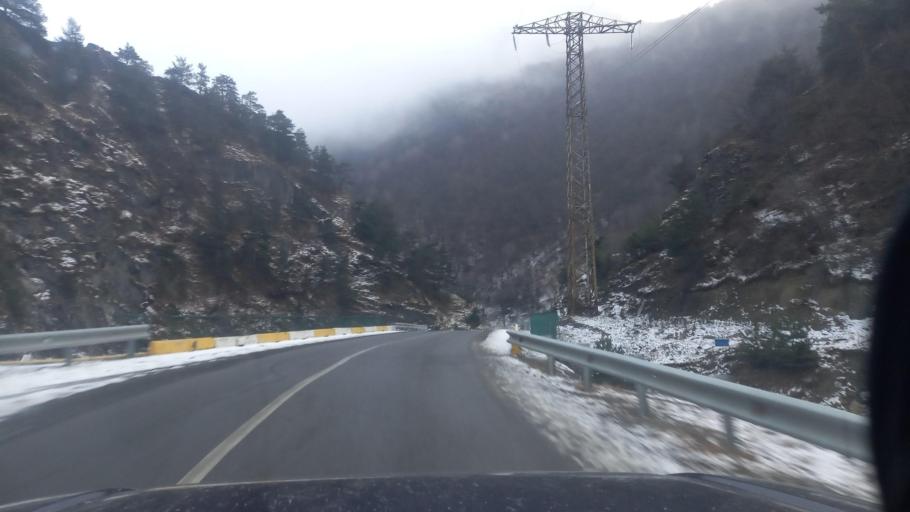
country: RU
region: Ingushetiya
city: Dzhayrakh
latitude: 42.7951
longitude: 44.7628
